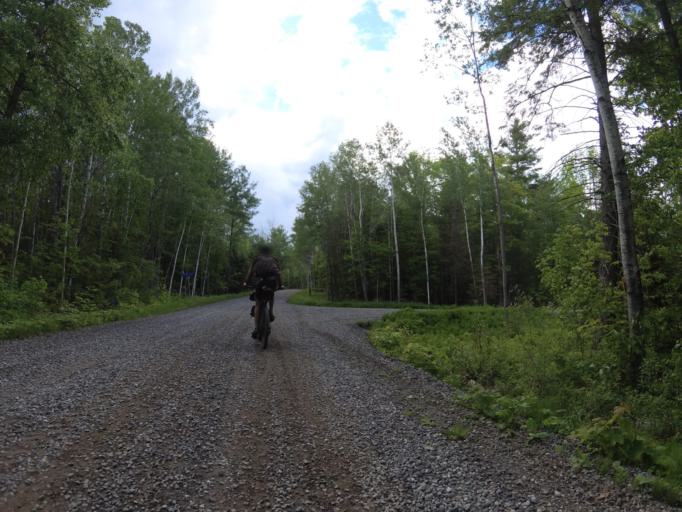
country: CA
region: Ontario
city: Renfrew
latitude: 45.1873
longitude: -76.8995
